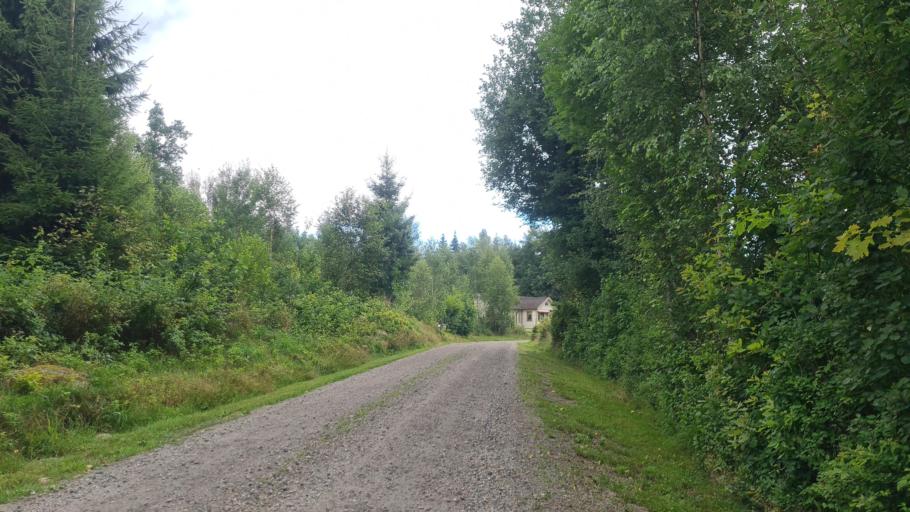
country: SE
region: Kronoberg
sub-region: Ljungby Kommun
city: Ljungby
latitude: 56.8215
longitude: 13.8633
